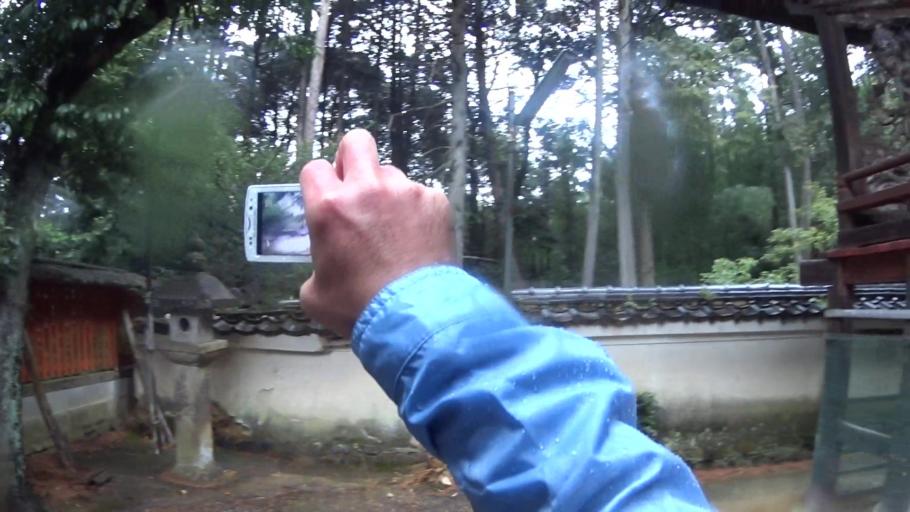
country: JP
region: Kyoto
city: Uji
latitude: 34.9542
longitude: 135.8225
